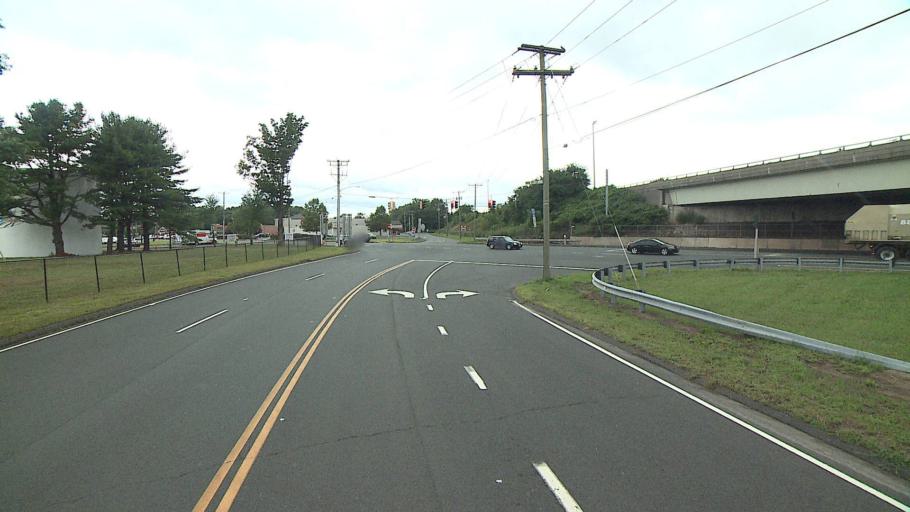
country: US
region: Connecticut
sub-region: Hartford County
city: Plainville
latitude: 41.6751
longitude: -72.8553
